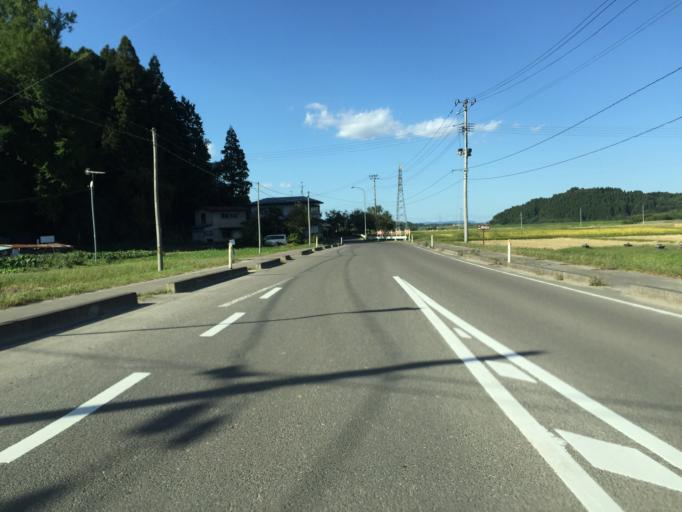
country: JP
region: Miyagi
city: Marumori
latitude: 37.8987
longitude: 140.7692
